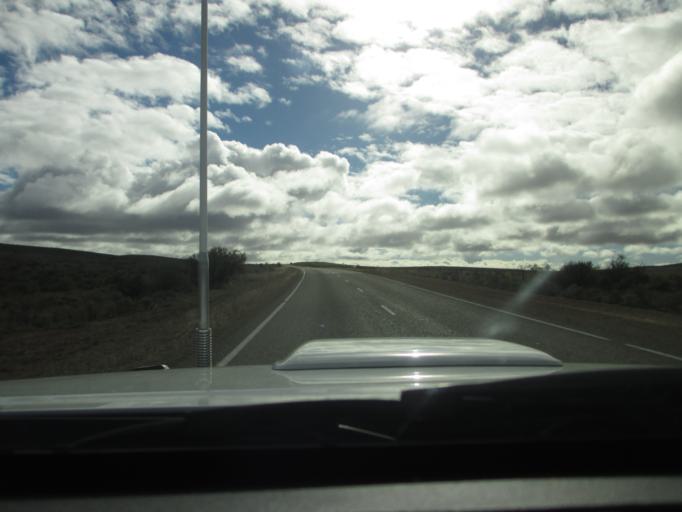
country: AU
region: South Australia
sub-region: Flinders Ranges
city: Quorn
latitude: -32.1922
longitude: 138.5343
